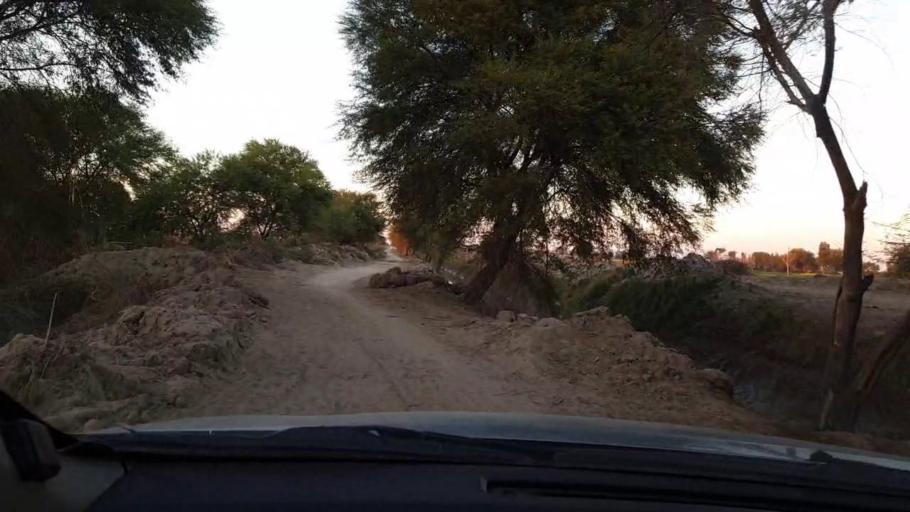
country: PK
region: Sindh
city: Jhol
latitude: 25.8982
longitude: 68.8867
